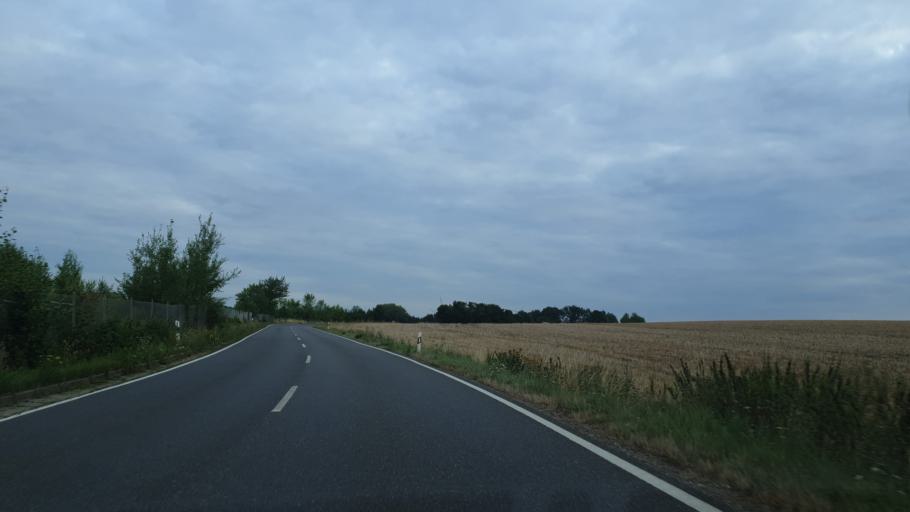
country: DE
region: Saxony
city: Sankt Egidien
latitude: 50.7988
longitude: 12.6175
